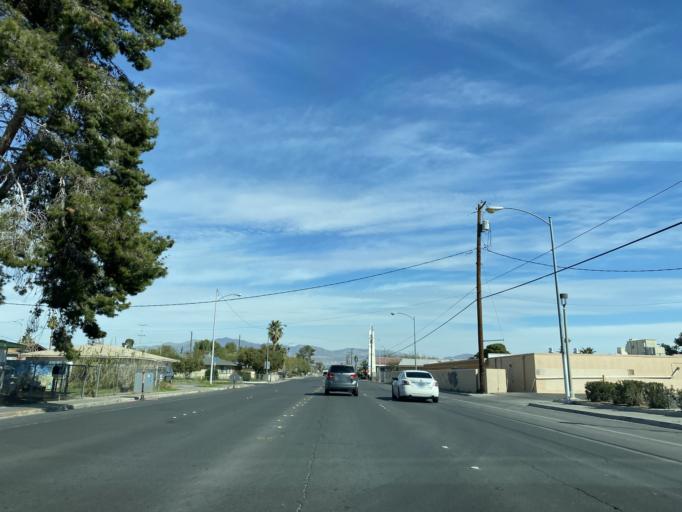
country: US
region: Nevada
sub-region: Clark County
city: North Las Vegas
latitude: 36.1906
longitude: -115.1251
